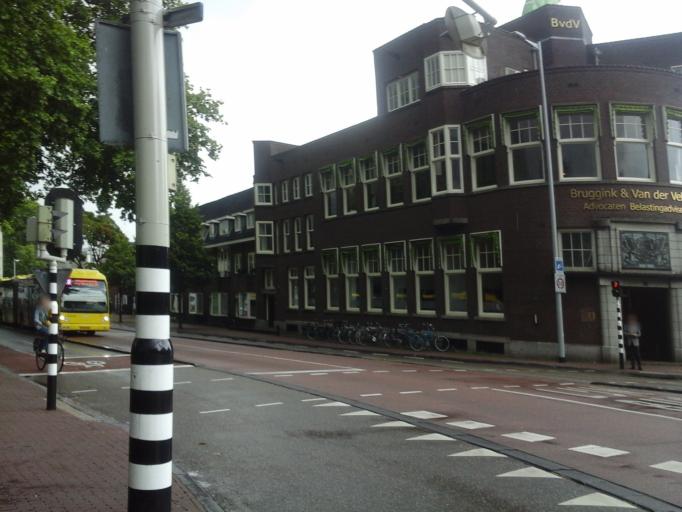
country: NL
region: Utrecht
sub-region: Gemeente Utrecht
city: Utrecht
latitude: 52.0929
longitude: 5.1278
